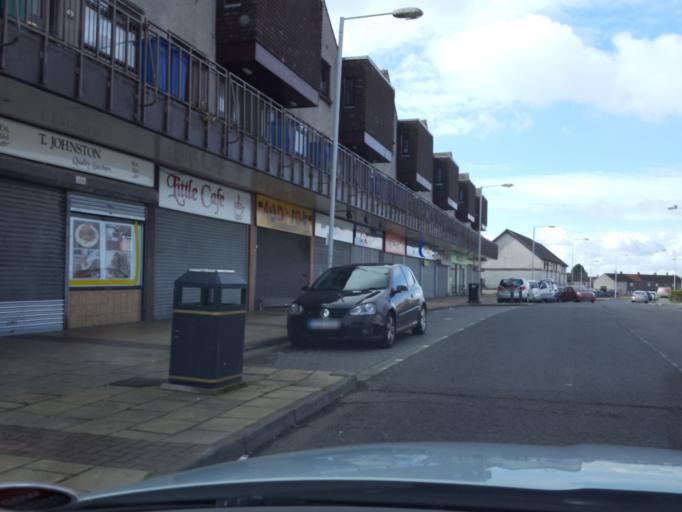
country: GB
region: Scotland
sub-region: Fife
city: Townhill
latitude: 56.0668
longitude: -3.4256
